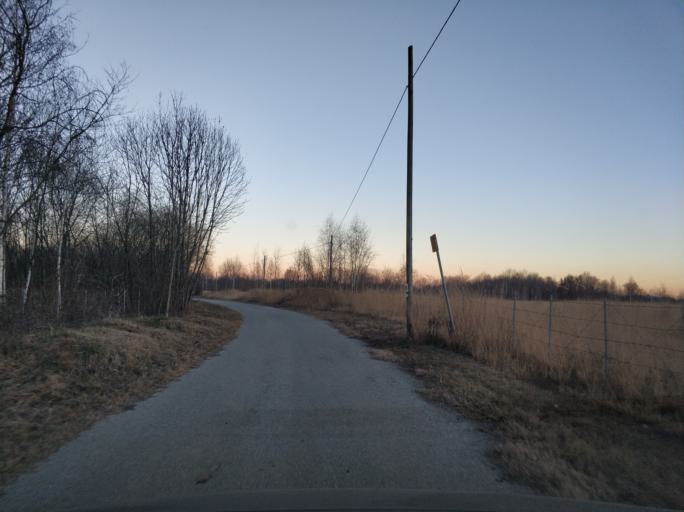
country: IT
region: Piedmont
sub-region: Provincia di Torino
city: Vauda Canavese Superiore
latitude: 45.2678
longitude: 7.6084
